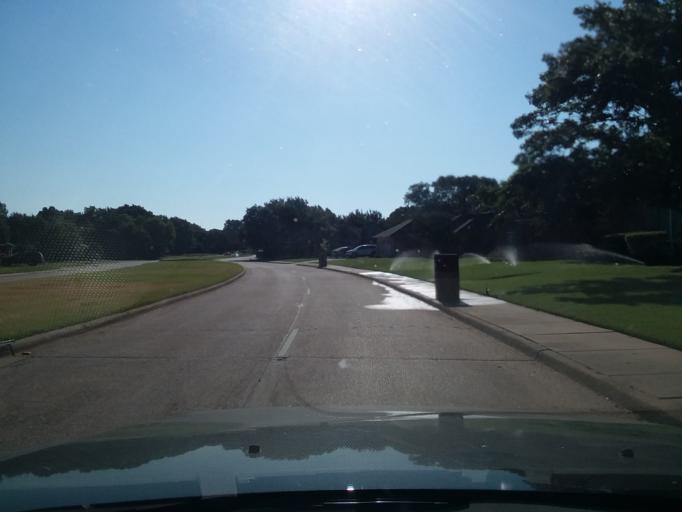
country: US
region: Texas
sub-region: Denton County
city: Highland Village
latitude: 33.0518
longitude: -97.0663
